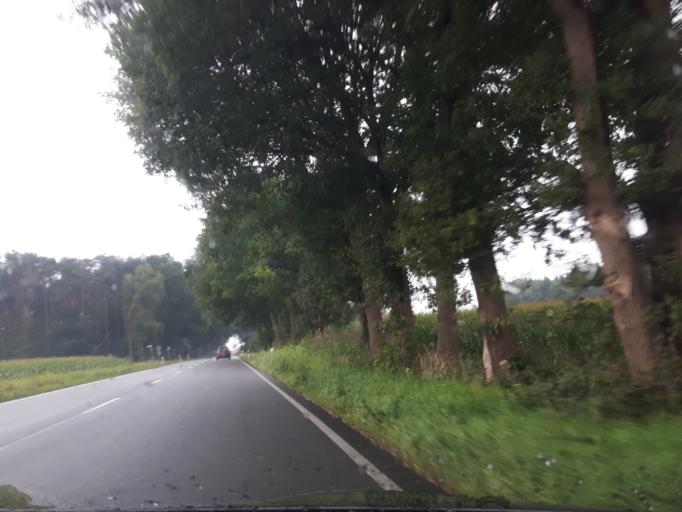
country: DE
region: Lower Saxony
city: Lingen
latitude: 52.4936
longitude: 7.2481
